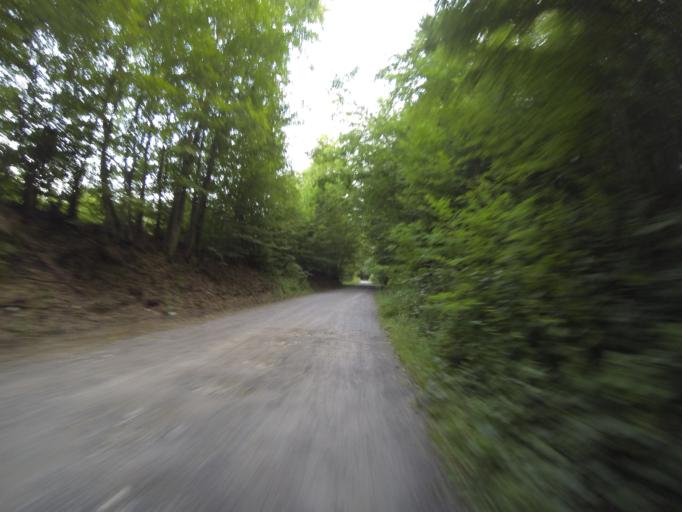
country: RO
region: Brasov
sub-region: Comuna Sinca Noua
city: Sinca Noua
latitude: 45.7291
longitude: 25.2843
